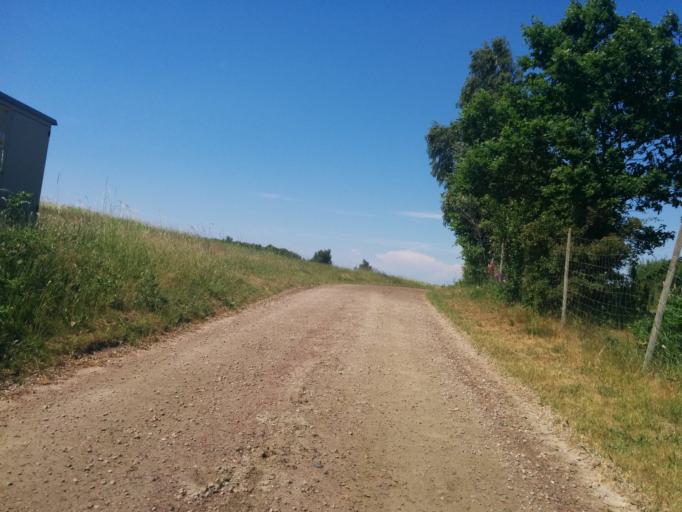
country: SE
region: Skane
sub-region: Lunds Kommun
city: Genarp
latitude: 55.5892
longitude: 13.3814
